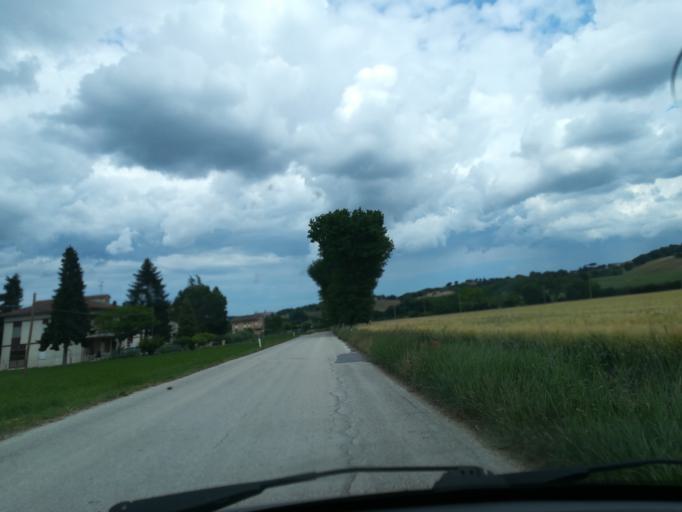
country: IT
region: The Marches
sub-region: Provincia di Macerata
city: Petriolo
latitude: 43.2342
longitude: 13.4611
